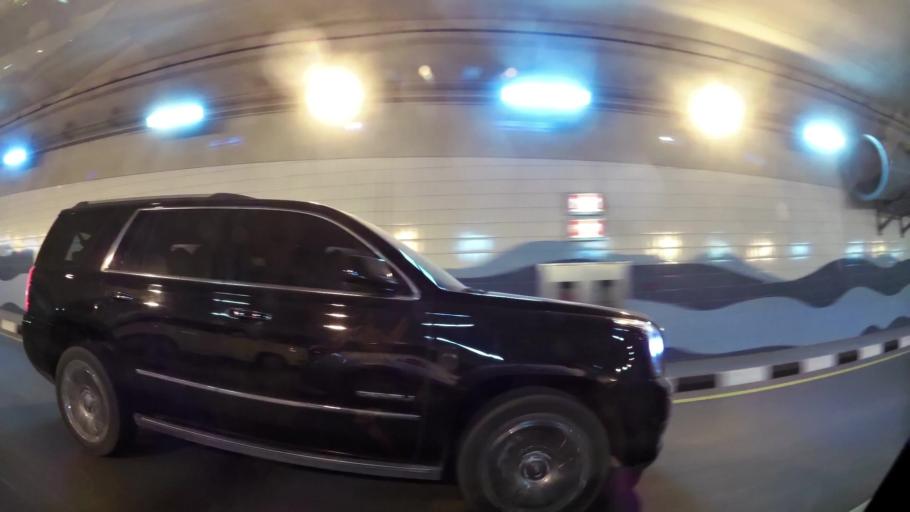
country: AE
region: Dubai
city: Dubai
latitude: 25.1252
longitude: 55.1174
